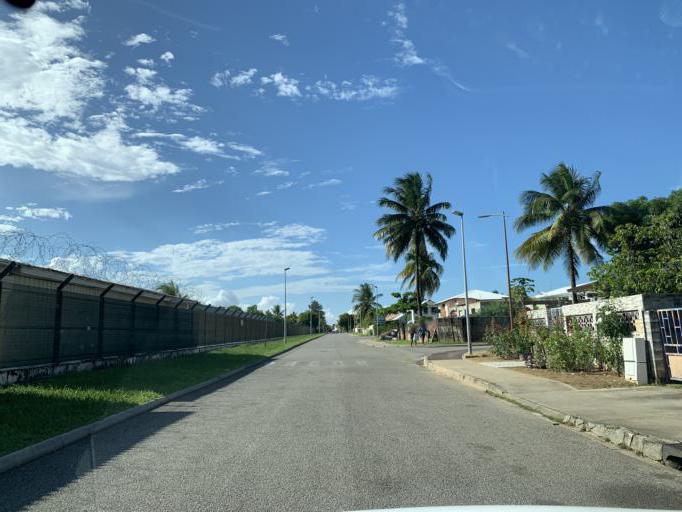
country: GF
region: Guyane
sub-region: Guyane
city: Kourou
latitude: 5.1717
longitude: -52.6458
